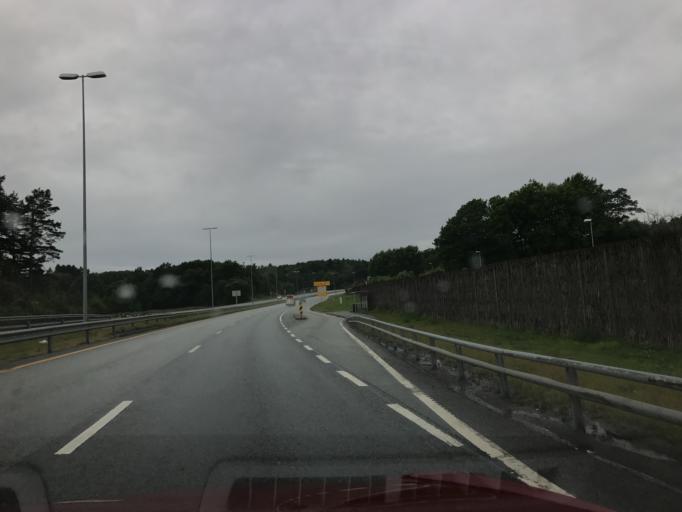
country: NO
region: Vest-Agder
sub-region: Kristiansand
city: Tveit
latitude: 58.1682
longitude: 8.1037
